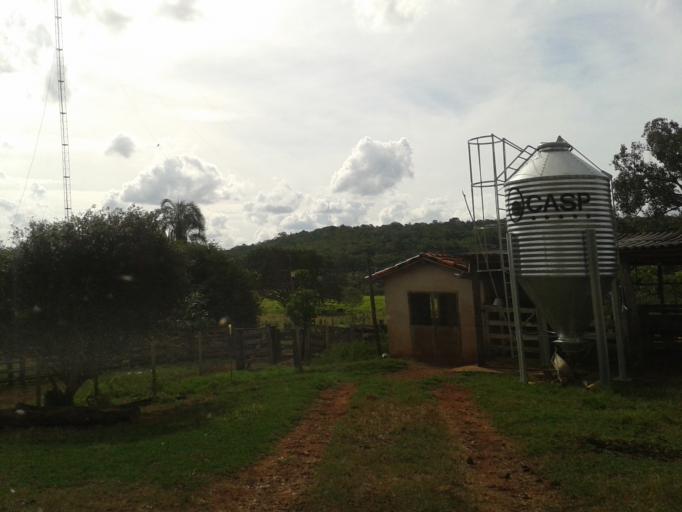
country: BR
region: Minas Gerais
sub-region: Campina Verde
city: Campina Verde
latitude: -19.4334
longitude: -49.6192
